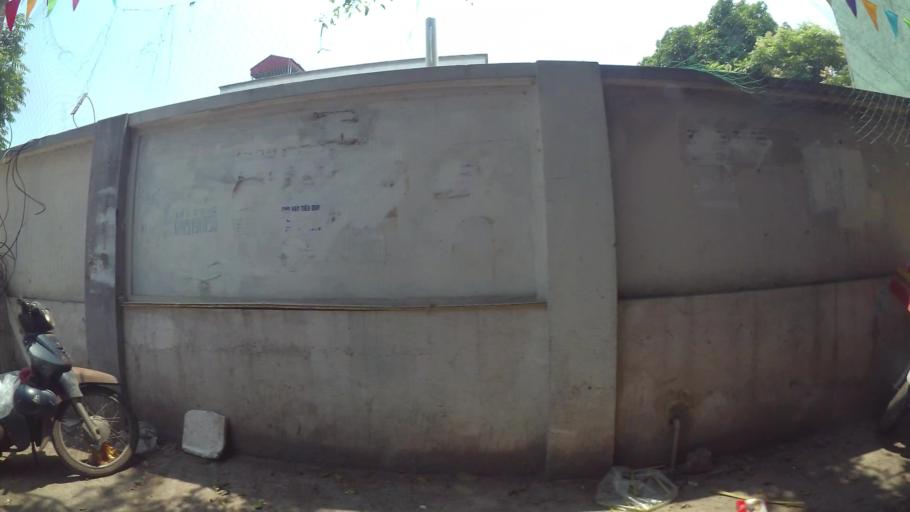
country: VN
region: Ha Noi
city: Hoan Kiem
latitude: 21.0229
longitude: 105.8921
